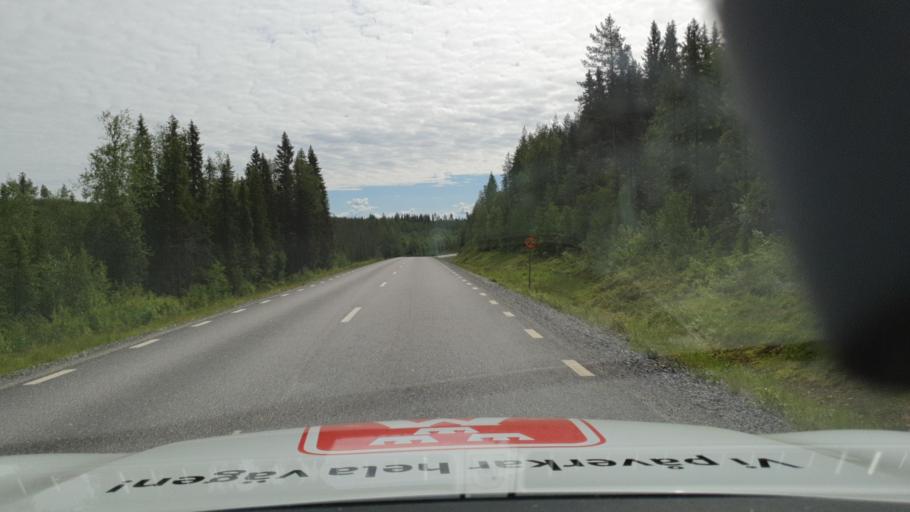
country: SE
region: Vaesterbotten
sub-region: Vindelns Kommun
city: Vindeln
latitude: 64.2540
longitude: 19.9562
